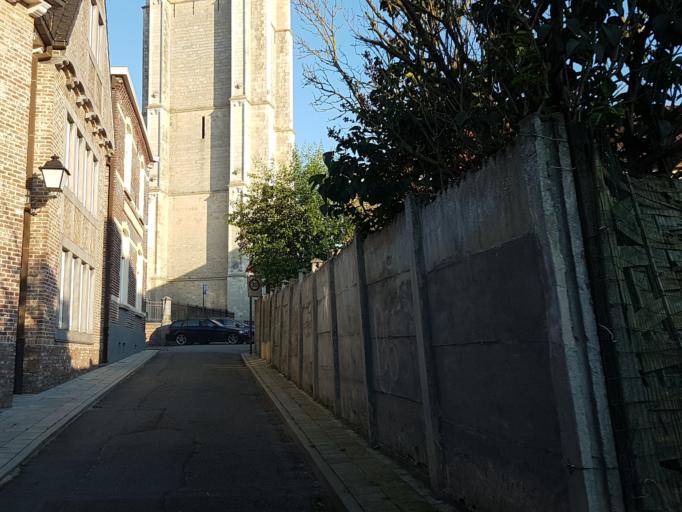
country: BE
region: Flanders
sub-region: Provincie Vlaams-Brabant
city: Ternat
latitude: 50.8724
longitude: 4.1757
